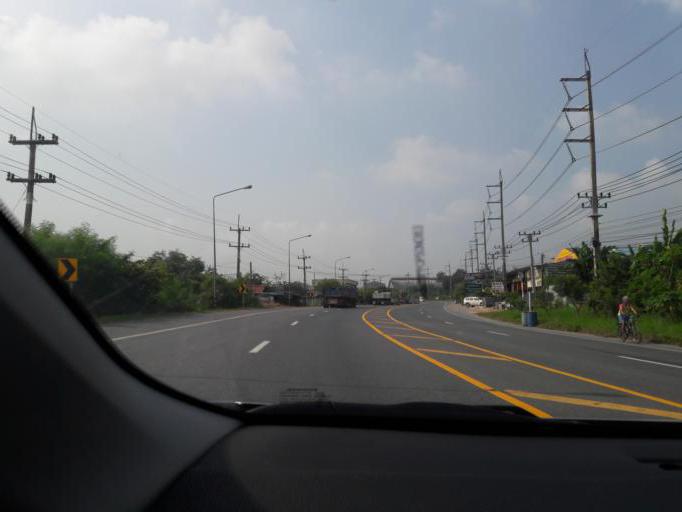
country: TH
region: Ang Thong
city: Ang Thong
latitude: 14.5683
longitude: 100.4536
